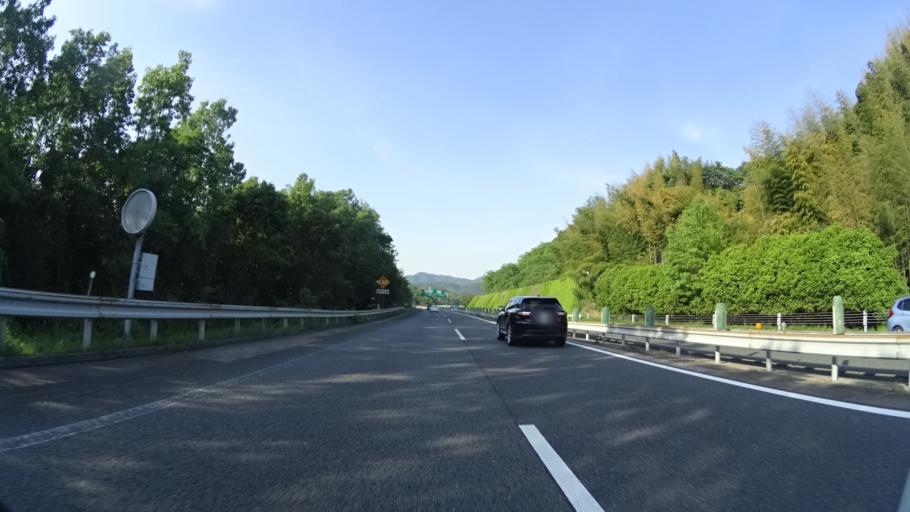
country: JP
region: Ehime
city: Kawanoecho
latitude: 33.9874
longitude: 133.5908
